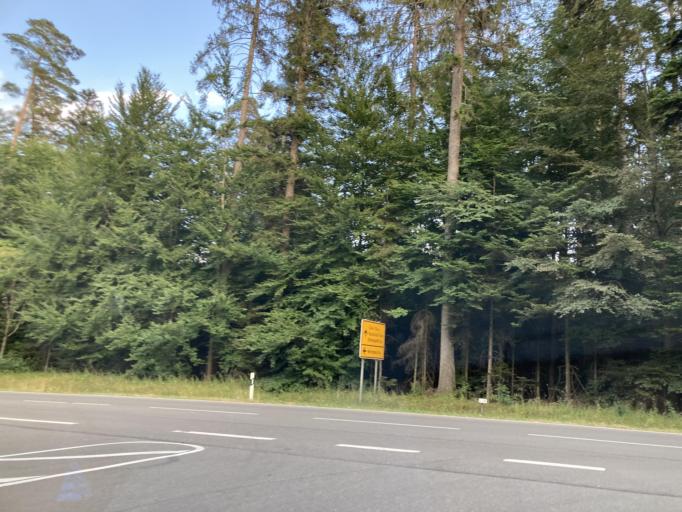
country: DE
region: Baden-Wuerttemberg
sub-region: Karlsruhe Region
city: Neubulach
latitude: 48.6421
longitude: 8.6677
